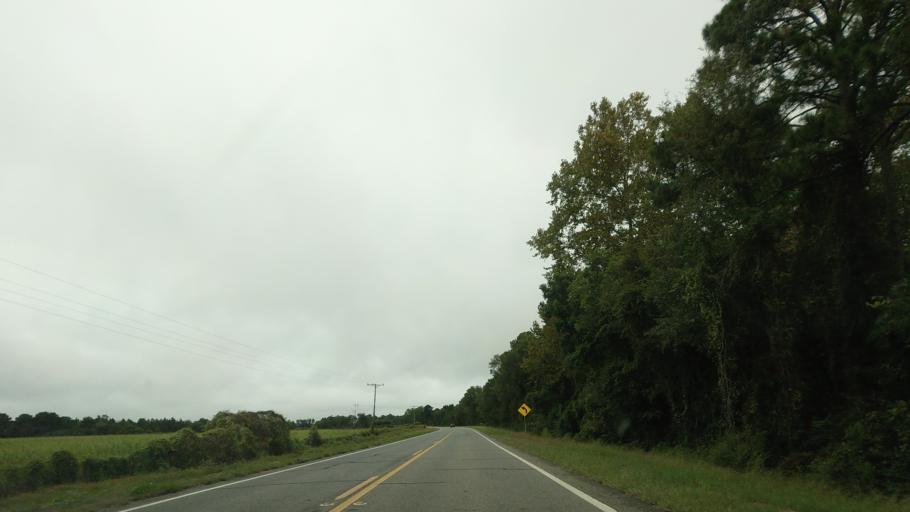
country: US
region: Georgia
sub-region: Irwin County
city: Ocilla
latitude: 31.5318
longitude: -83.2475
